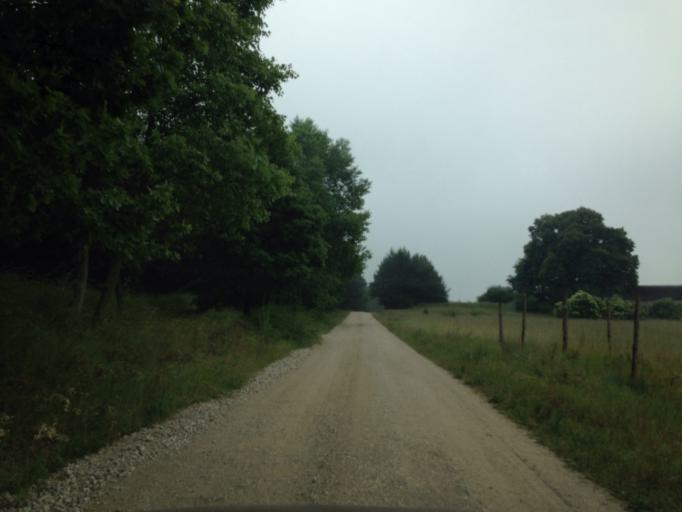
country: PL
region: Kujawsko-Pomorskie
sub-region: Powiat brodnicki
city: Bobrowo
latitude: 53.3571
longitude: 19.3044
